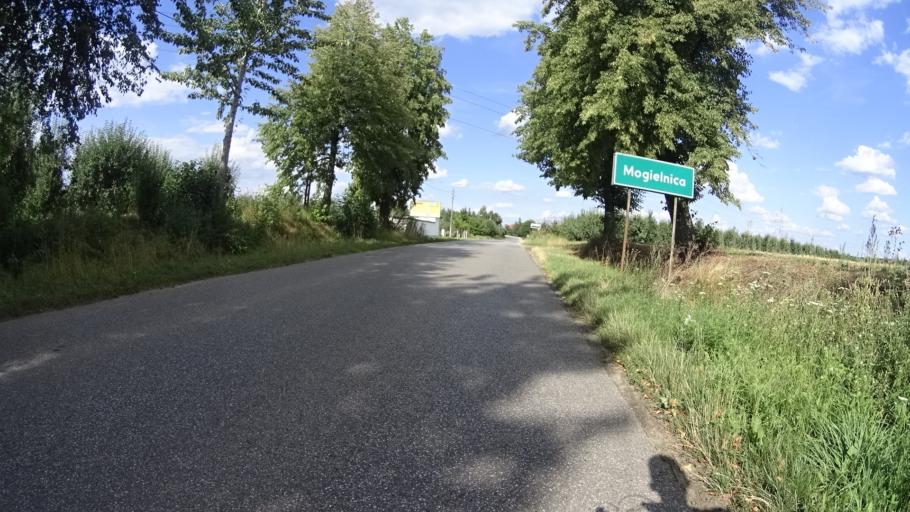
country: PL
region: Masovian Voivodeship
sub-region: Powiat grojecki
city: Mogielnica
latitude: 51.6825
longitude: 20.7149
